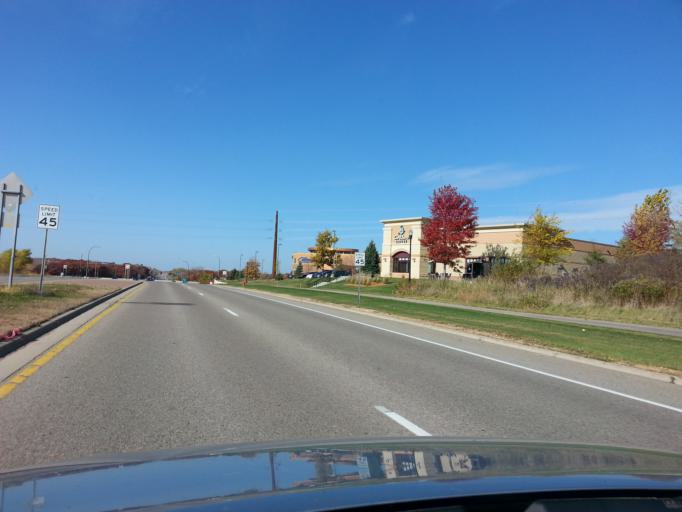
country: US
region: Minnesota
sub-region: Dakota County
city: Lakeville
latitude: 44.6814
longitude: -93.2874
